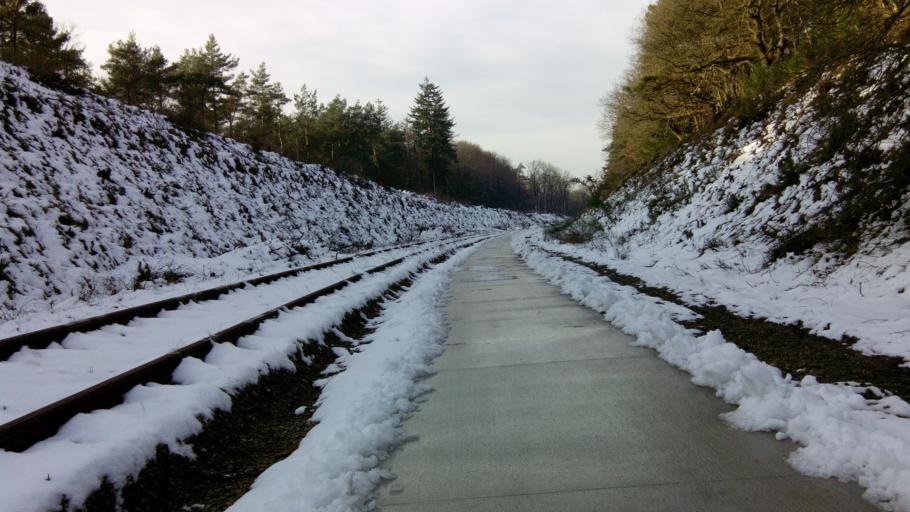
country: NL
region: Gelderland
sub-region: Gemeente Groesbeek
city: Groesbeek
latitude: 51.7752
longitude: 5.9022
